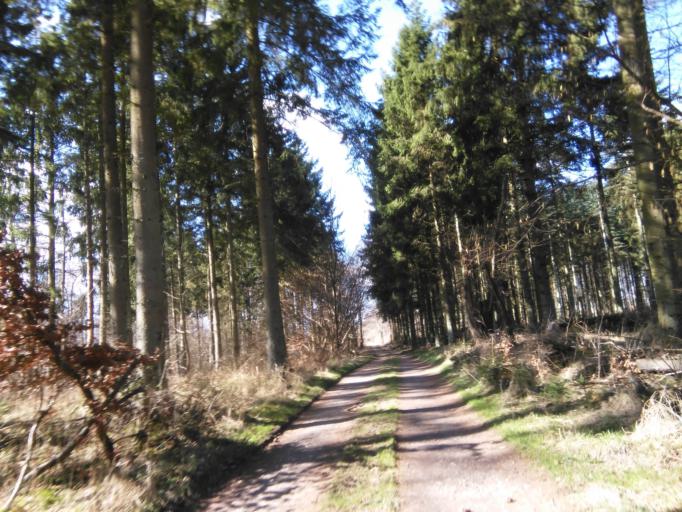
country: DK
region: Central Jutland
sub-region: Skanderborg Kommune
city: Ry
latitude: 56.0482
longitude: 9.7157
